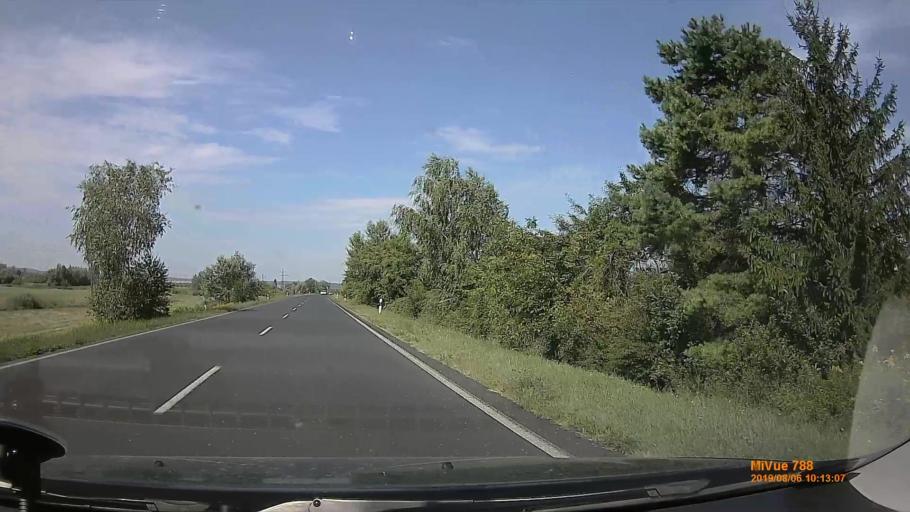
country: HU
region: Somogy
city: Balatonfenyves
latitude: 46.7008
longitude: 17.4427
